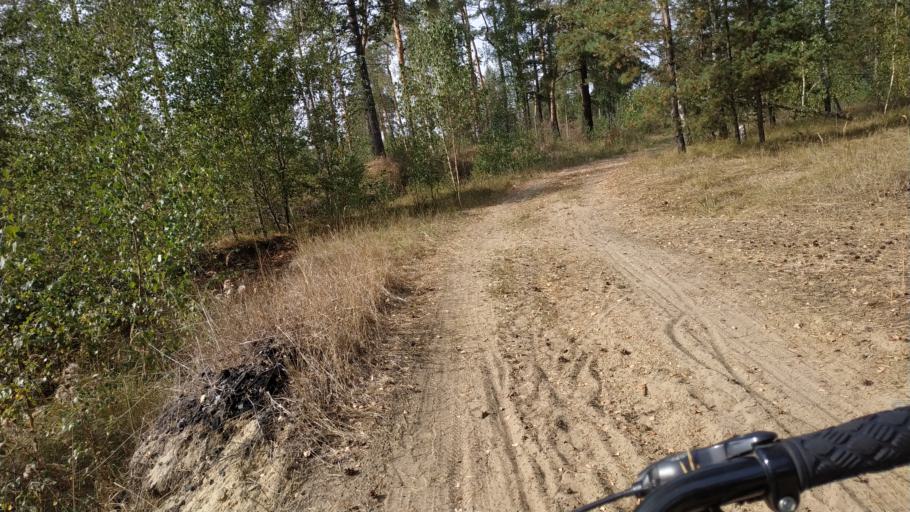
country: RU
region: Moskovskaya
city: Malyshevo
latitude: 55.5320
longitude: 38.2937
